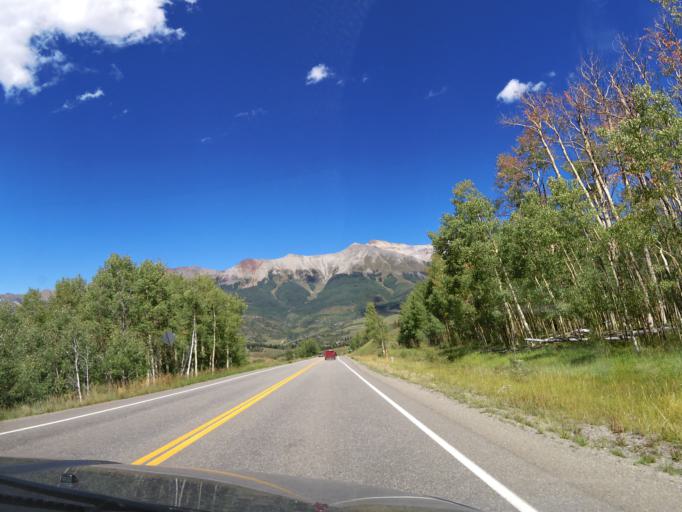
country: US
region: Colorado
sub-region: San Miguel County
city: Mountain Village
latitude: 37.9278
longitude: -107.8820
